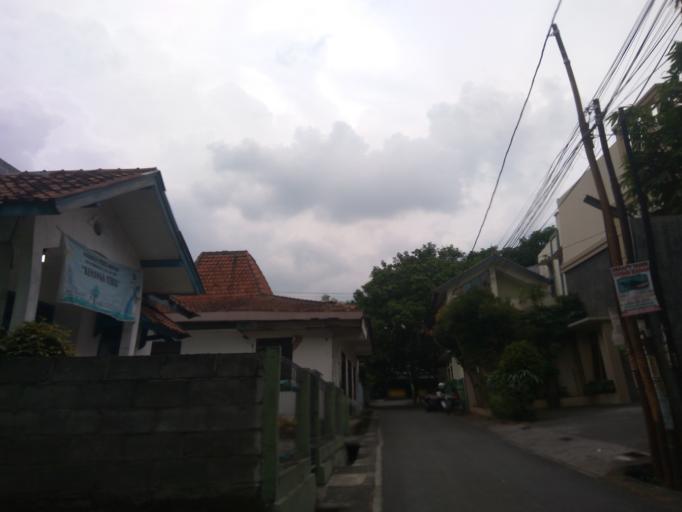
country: ID
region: Central Java
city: Semarang
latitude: -7.0633
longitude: 110.4417
